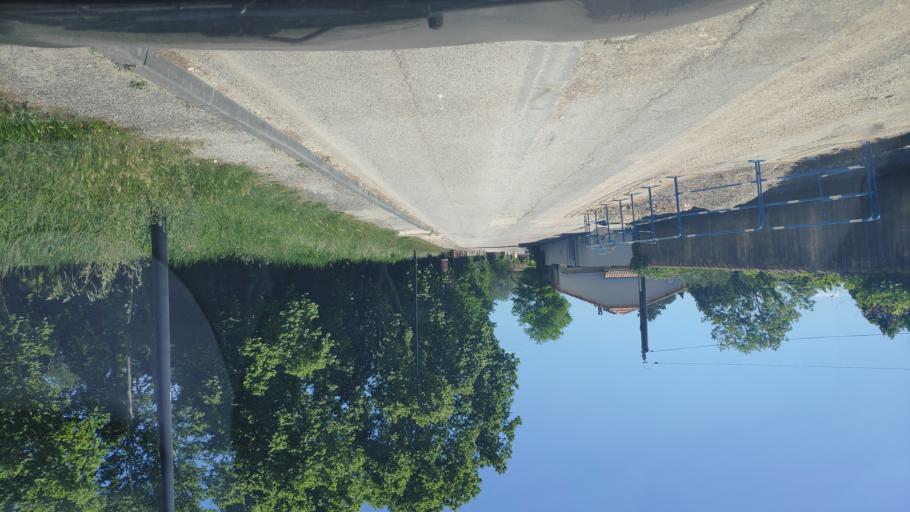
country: FR
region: Provence-Alpes-Cote d'Azur
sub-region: Departement du Vaucluse
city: Loriol-du-Comtat
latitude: 44.0749
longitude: 5.0042
